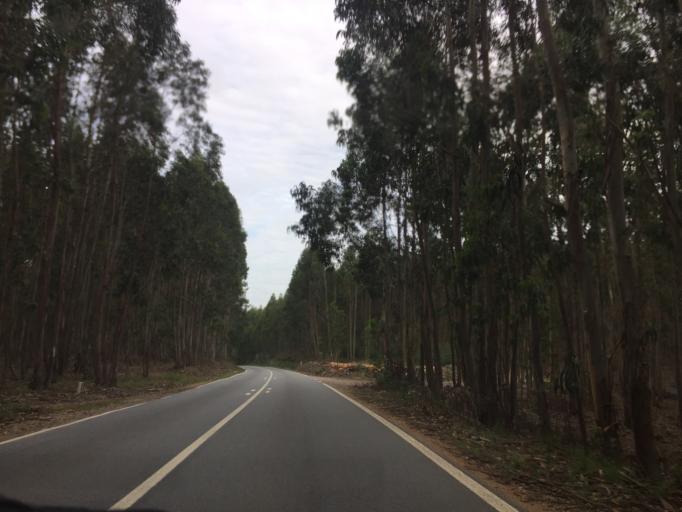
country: PT
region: Aveiro
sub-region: Agueda
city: Aguada de Cima
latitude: 40.4968
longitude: -8.3542
